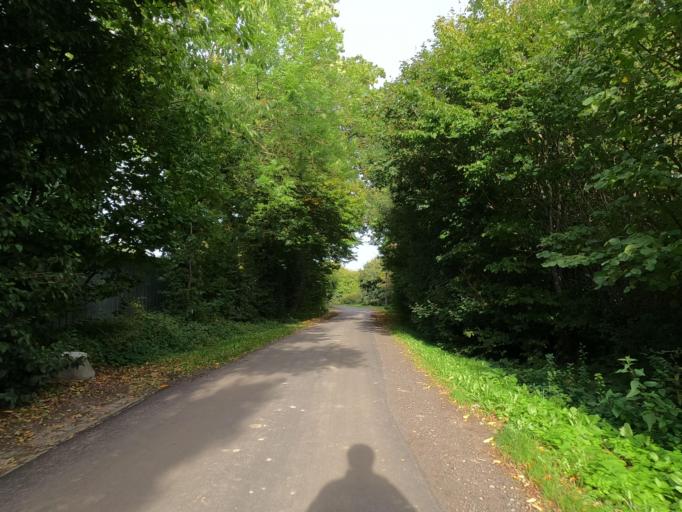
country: DE
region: Schleswig-Holstein
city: Grube
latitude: 54.2232
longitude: 11.0330
